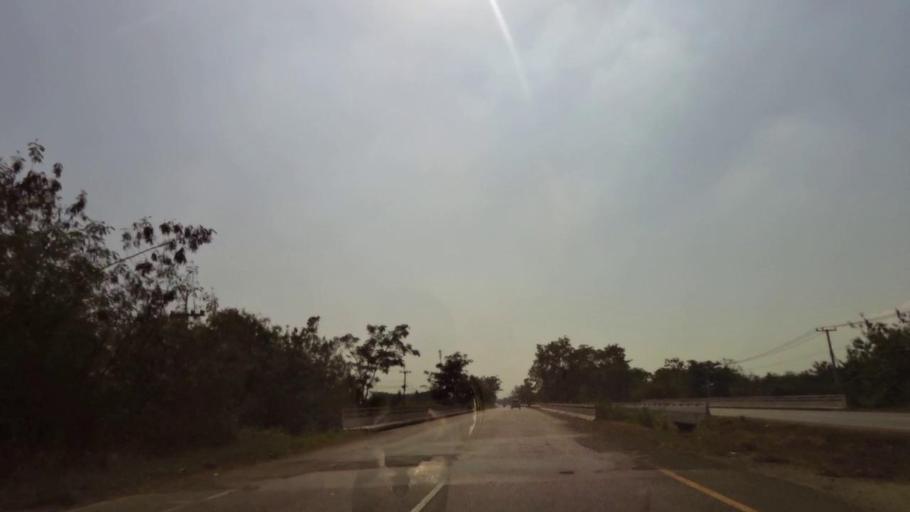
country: TH
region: Phichit
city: Wachira Barami
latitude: 16.3629
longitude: 100.1305
